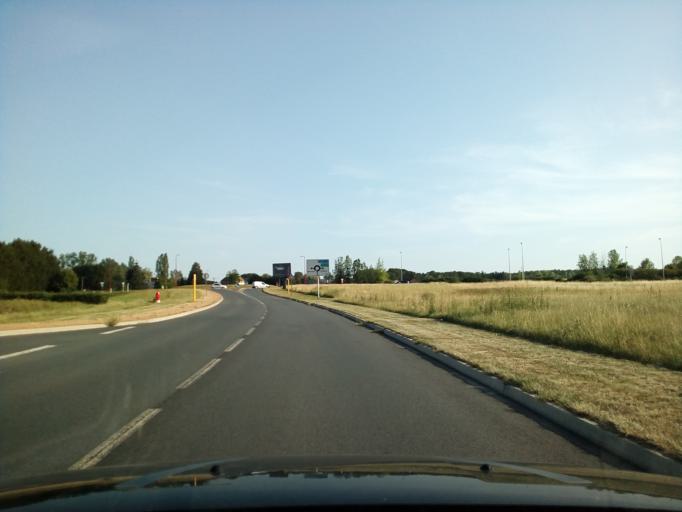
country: FR
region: Auvergne
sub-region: Departement de l'Allier
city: Domerat
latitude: 46.3598
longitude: 2.5524
